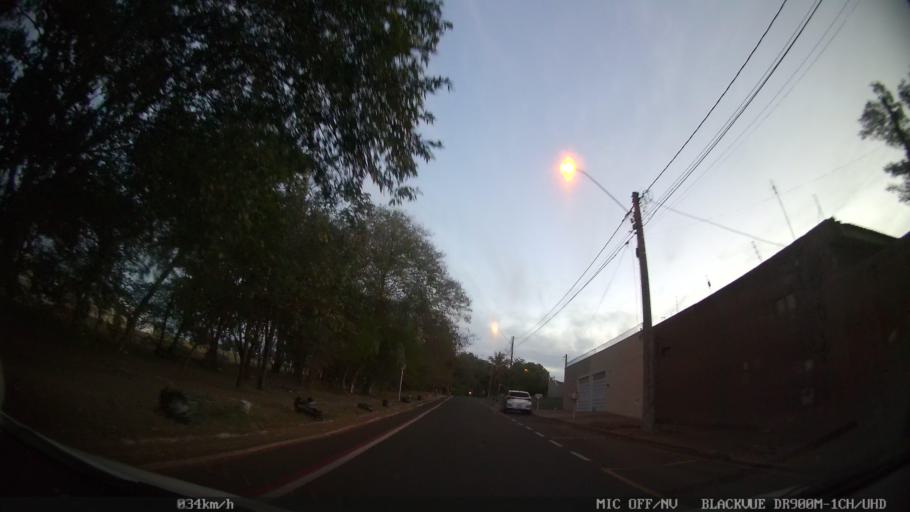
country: BR
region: Sao Paulo
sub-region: Catanduva
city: Catanduva
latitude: -21.1490
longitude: -48.9933
